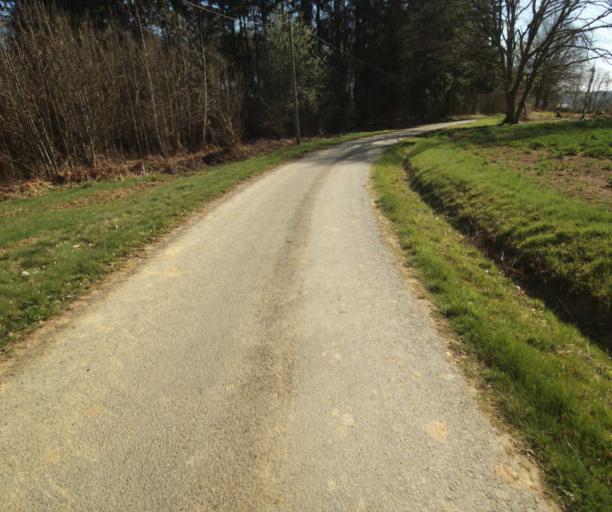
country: FR
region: Limousin
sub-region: Departement de la Correze
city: Chamboulive
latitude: 45.4318
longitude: 1.6656
